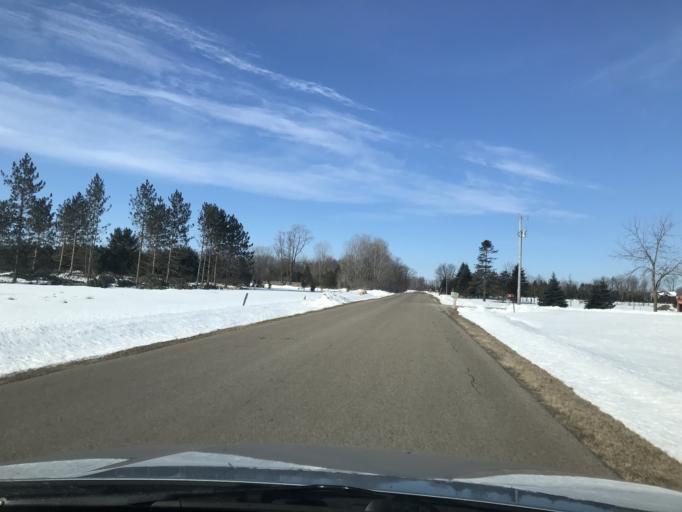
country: US
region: Wisconsin
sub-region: Oconto County
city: Oconto Falls
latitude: 44.9233
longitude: -88.1769
